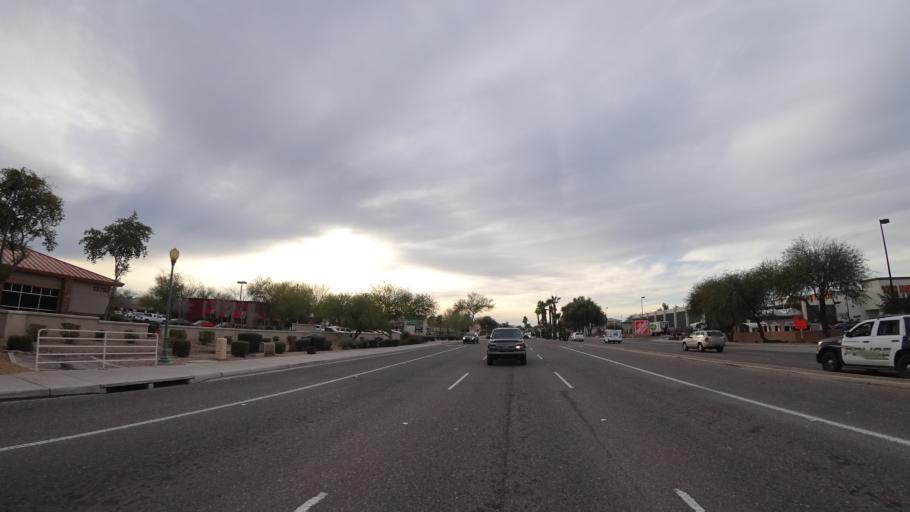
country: US
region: Arizona
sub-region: Maricopa County
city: Surprise
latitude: 33.6386
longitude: -112.3556
